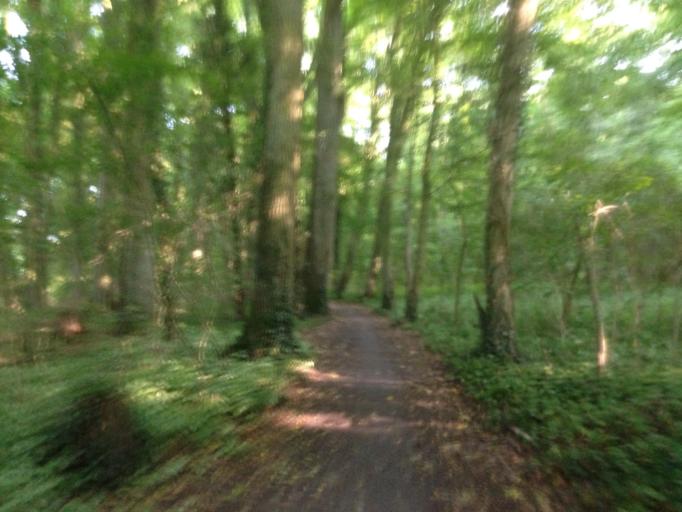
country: DE
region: North Rhine-Westphalia
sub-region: Regierungsbezirk Munster
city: Muenster
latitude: 52.0085
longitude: 7.5699
